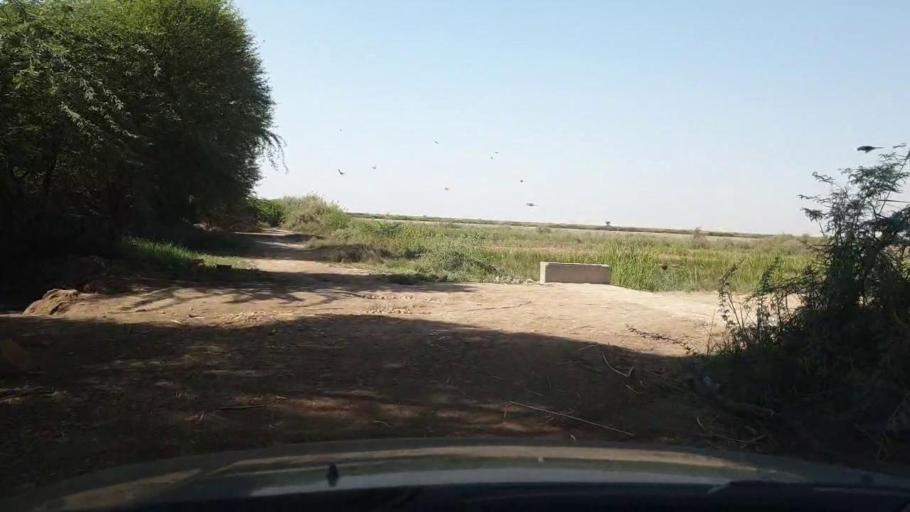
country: PK
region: Sindh
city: Daro Mehar
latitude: 24.9758
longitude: 68.1014
